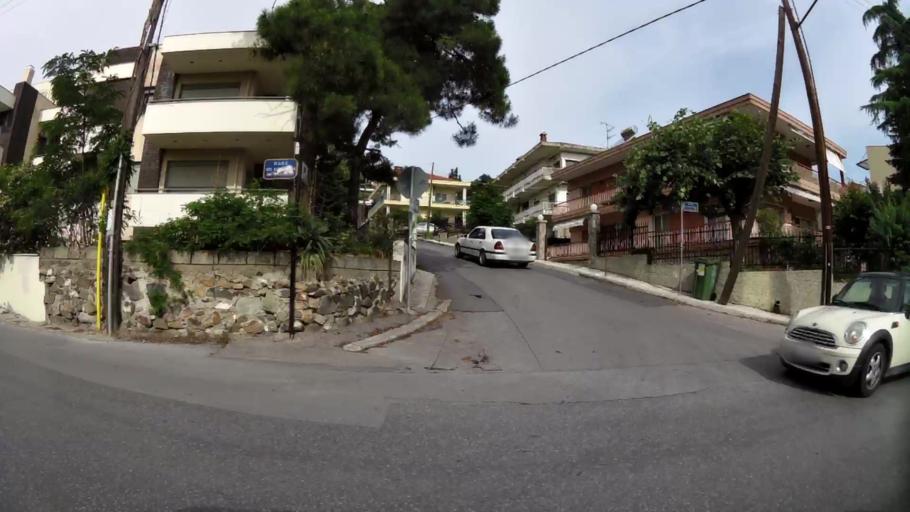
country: GR
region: Central Macedonia
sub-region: Nomos Thessalonikis
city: Panorama
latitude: 40.5885
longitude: 23.0353
